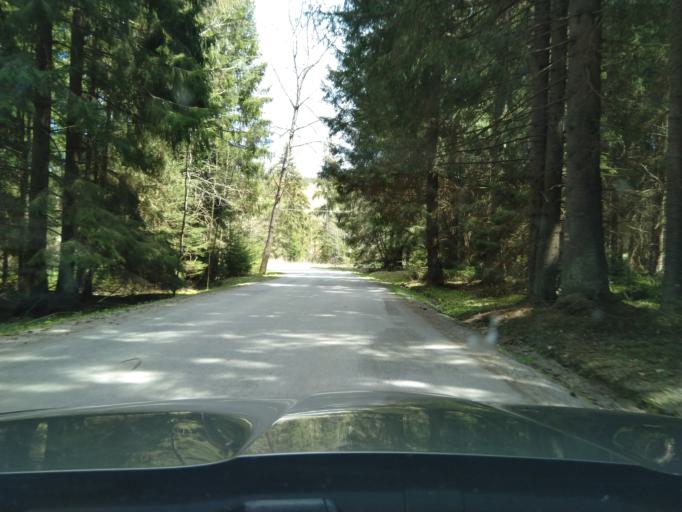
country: CZ
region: Jihocesky
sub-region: Okres Prachatice
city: Vimperk
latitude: 49.0171
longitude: 13.7279
